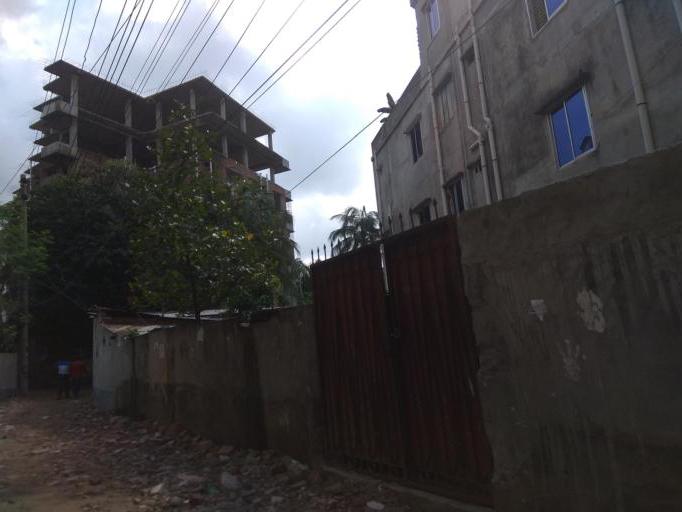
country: BD
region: Dhaka
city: Tungi
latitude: 23.8124
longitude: 90.3880
